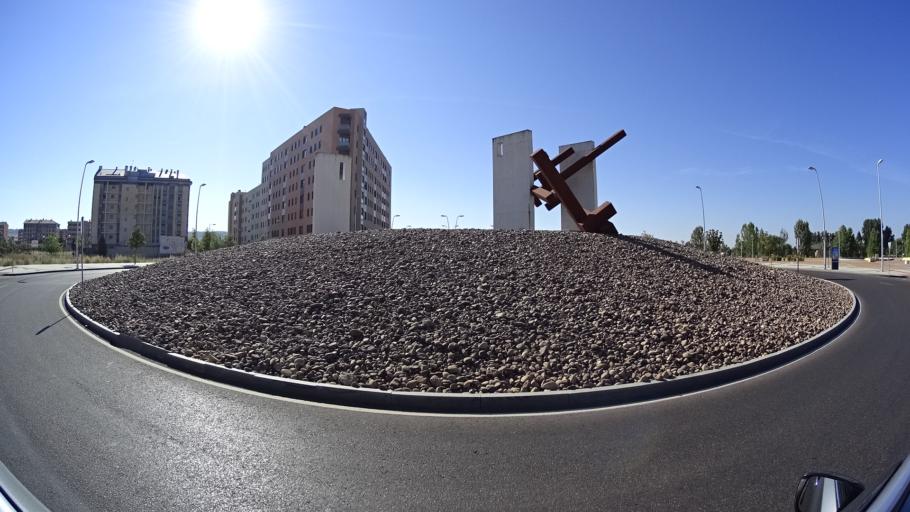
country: ES
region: Castille and Leon
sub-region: Provincia de Leon
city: Leon
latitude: 42.5819
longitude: -5.5653
